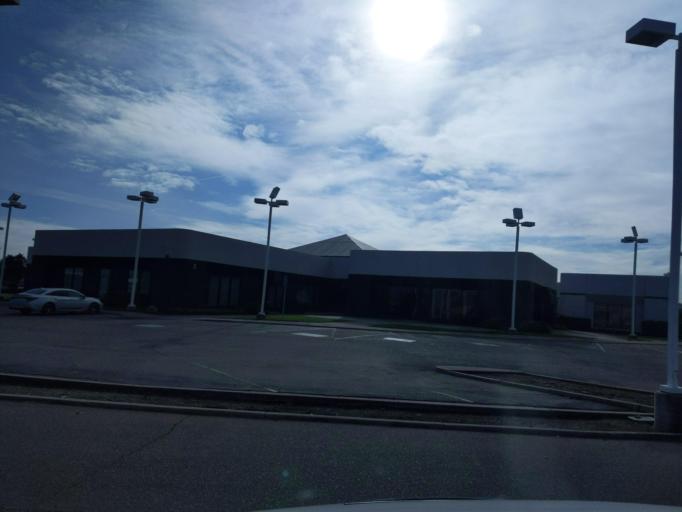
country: US
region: California
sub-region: San Joaquin County
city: Morada
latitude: 38.0189
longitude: -121.2766
